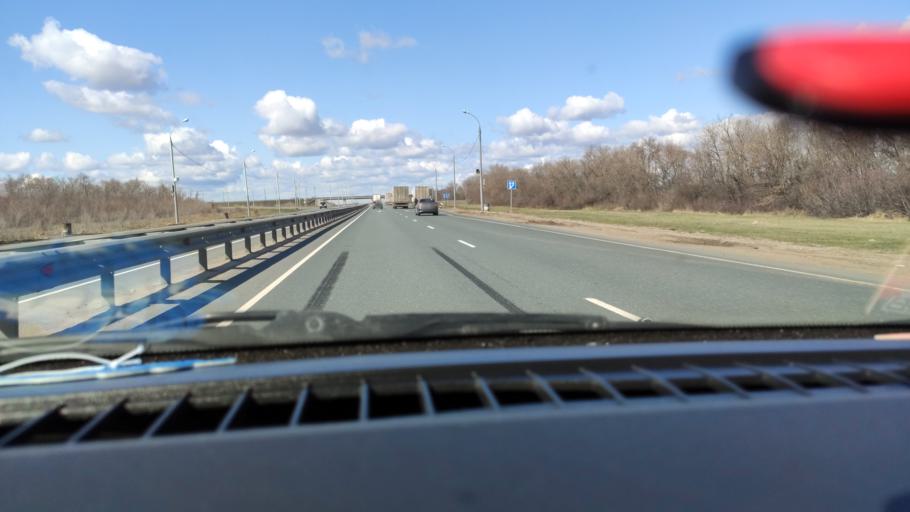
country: RU
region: Samara
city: Varlamovo
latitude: 53.1968
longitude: 48.2953
